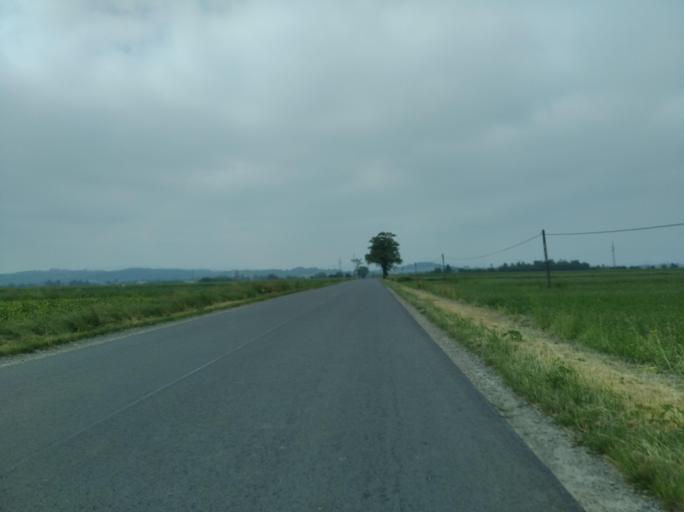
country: PL
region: Subcarpathian Voivodeship
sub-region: Powiat brzozowski
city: Haczow
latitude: 49.6253
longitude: 21.9091
